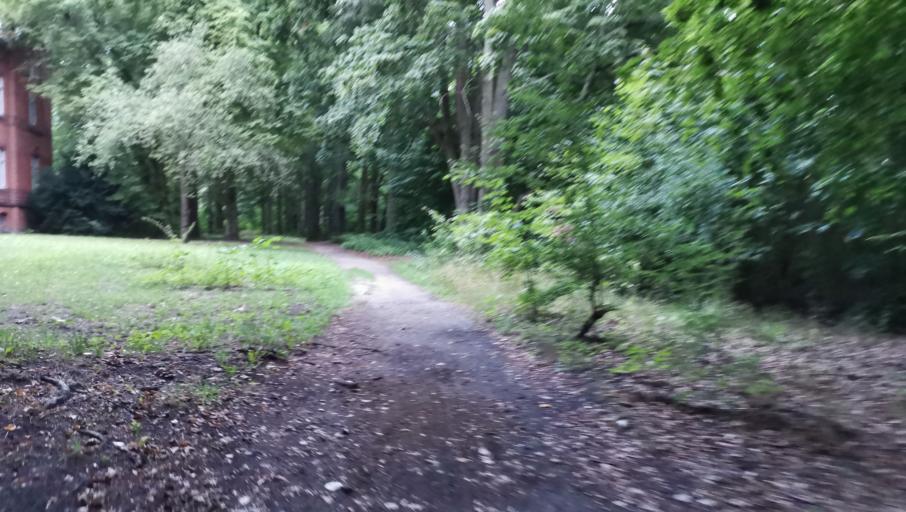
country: DE
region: Brandenburg
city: Potsdam
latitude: 52.3817
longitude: 13.0297
